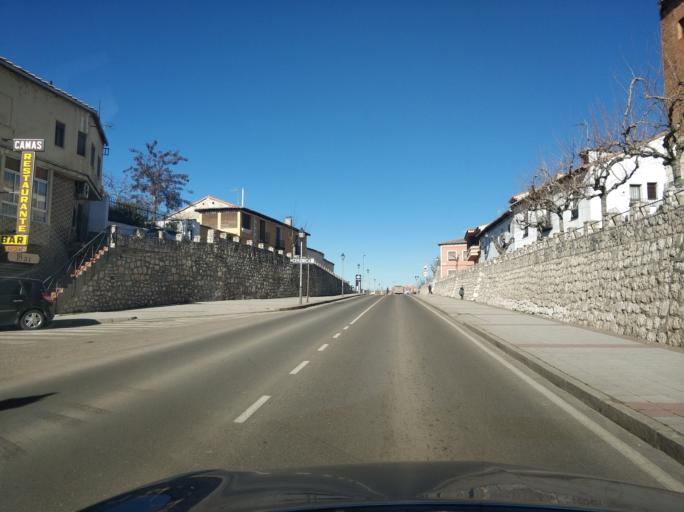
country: ES
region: Castille and Leon
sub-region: Provincia de Valladolid
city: Tordesillas
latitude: 41.4998
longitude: -5.0030
